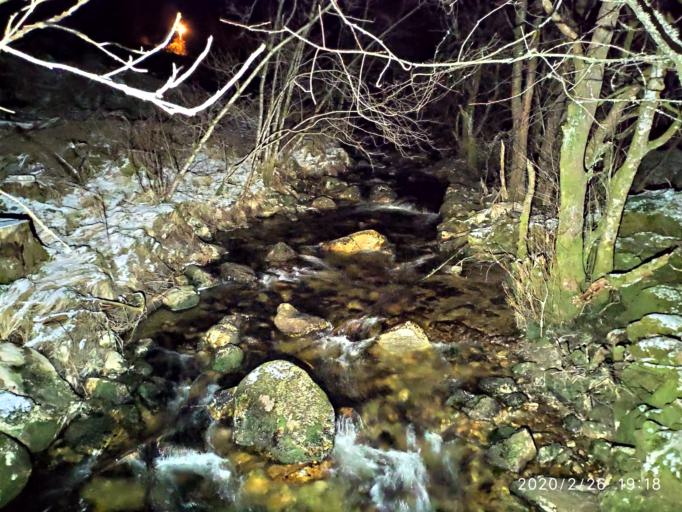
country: NO
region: Hordaland
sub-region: Tysnes
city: Uggdal
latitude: 60.0150
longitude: 5.5368
